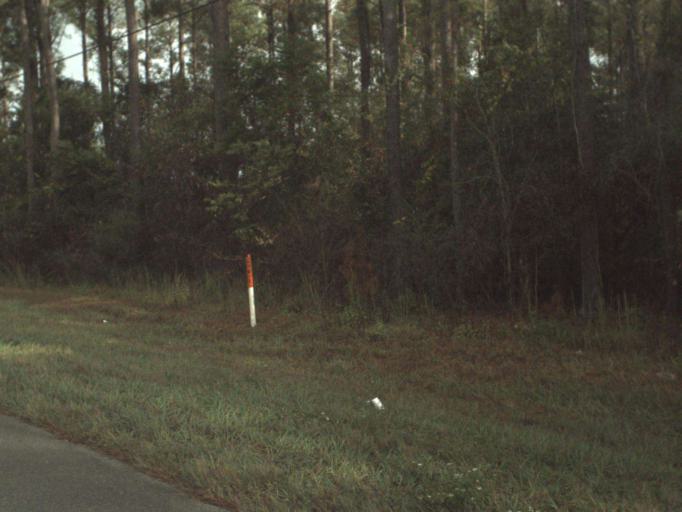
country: US
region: Florida
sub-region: Gadsden County
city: Havana
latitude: 30.6441
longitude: -84.4168
